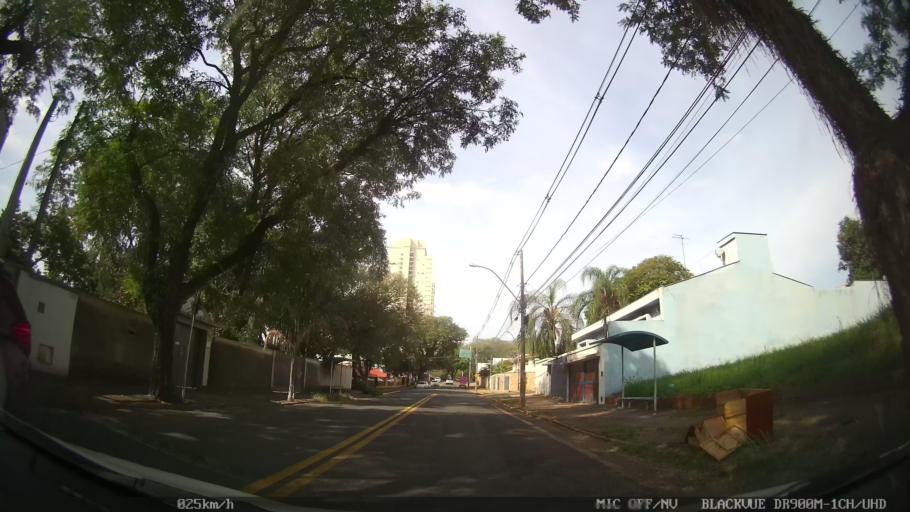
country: BR
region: Sao Paulo
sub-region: Piracicaba
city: Piracicaba
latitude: -22.7168
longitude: -47.6628
